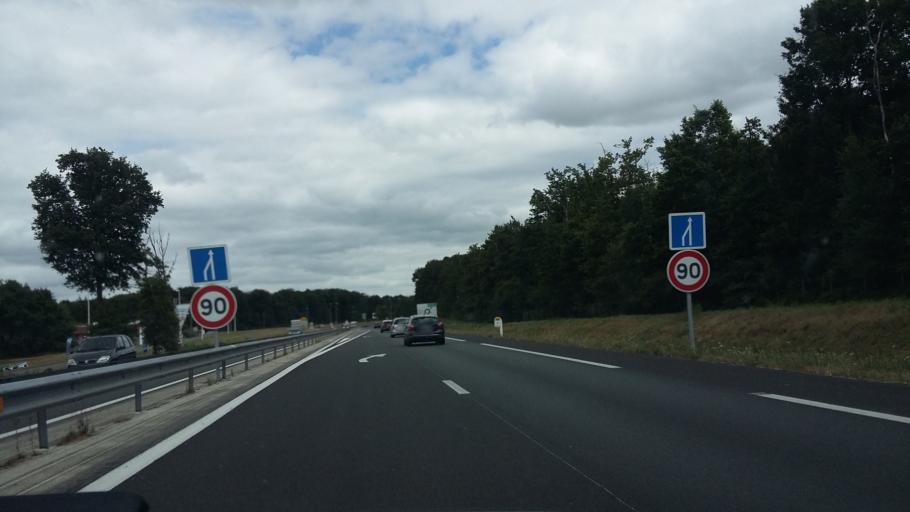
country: FR
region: Pays de la Loire
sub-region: Departement de la Vendee
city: Aizenay
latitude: 46.7323
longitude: -1.5937
